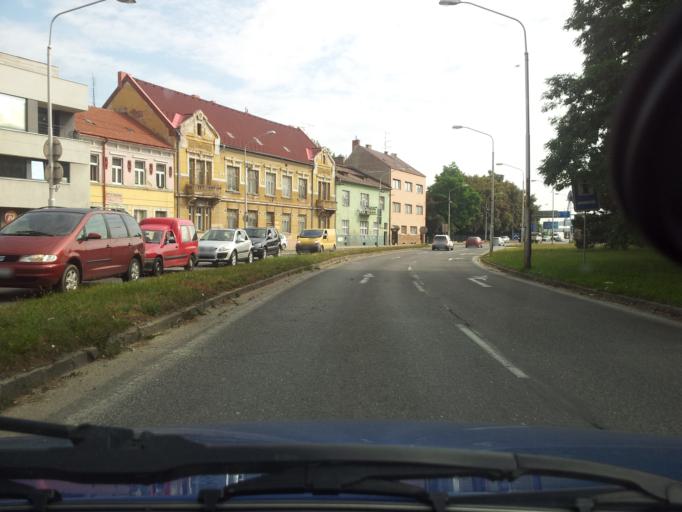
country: SK
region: Trenciansky
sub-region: Okres Trencin
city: Trencin
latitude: 48.8949
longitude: 18.0380
